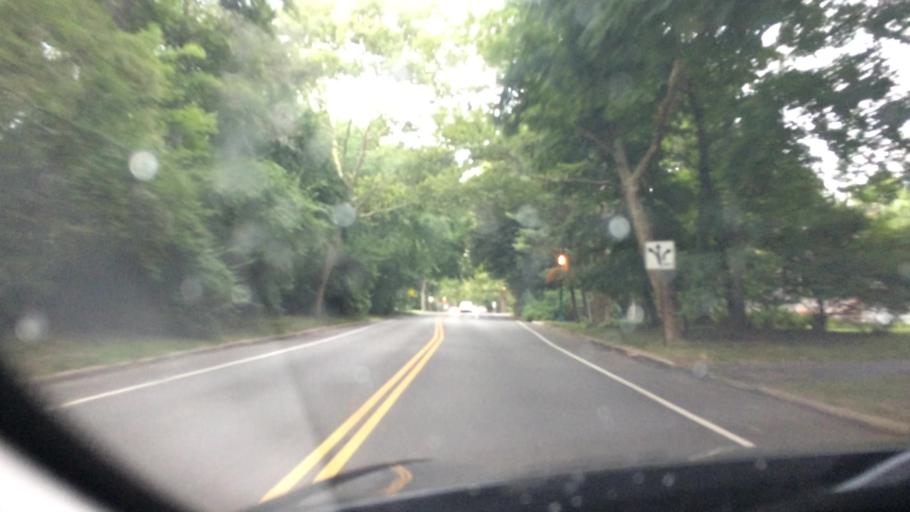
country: US
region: Ohio
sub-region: Lucas County
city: Ottawa Hills
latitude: 41.6722
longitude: -83.6438
